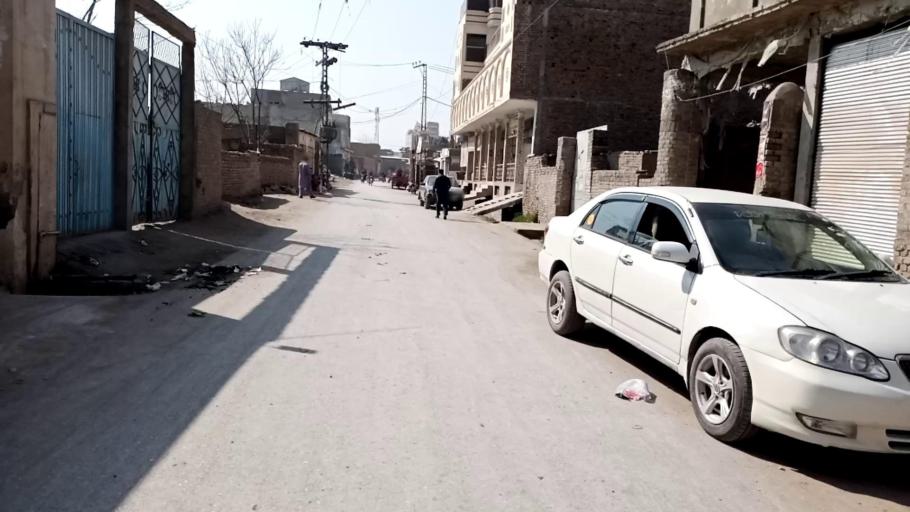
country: PK
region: Khyber Pakhtunkhwa
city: Peshawar
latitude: 34.0112
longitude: 71.5113
